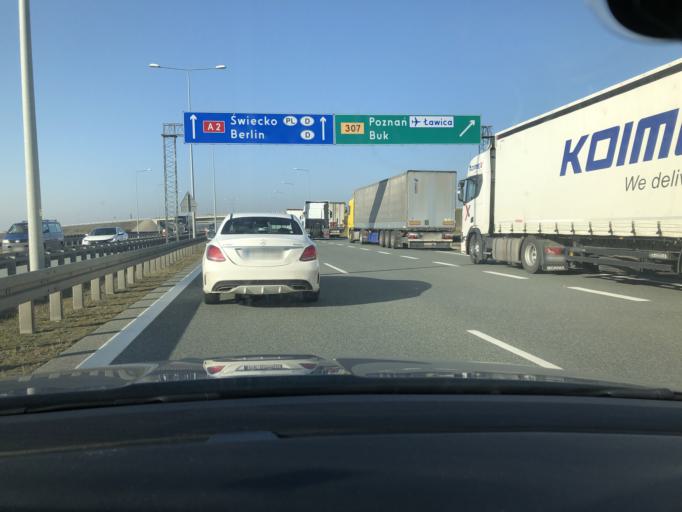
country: PL
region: Greater Poland Voivodeship
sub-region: Powiat poznanski
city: Buk
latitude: 52.3756
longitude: 16.5698
